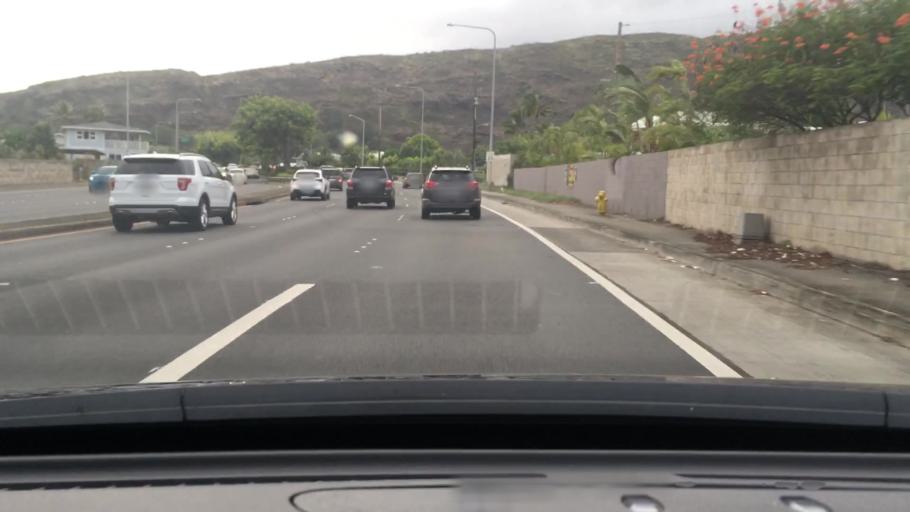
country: US
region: Hawaii
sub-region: Honolulu County
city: Waimanalo Beach
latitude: 21.2860
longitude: -157.7198
